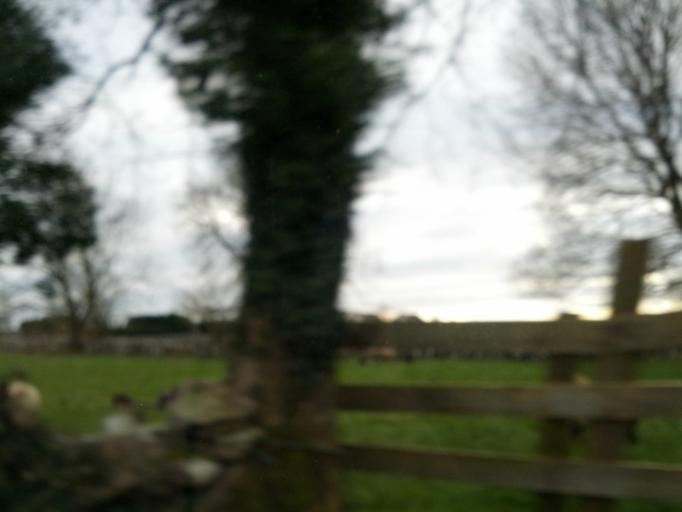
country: IE
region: Connaught
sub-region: County Galway
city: Oranmore
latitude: 53.2118
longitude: -8.8523
